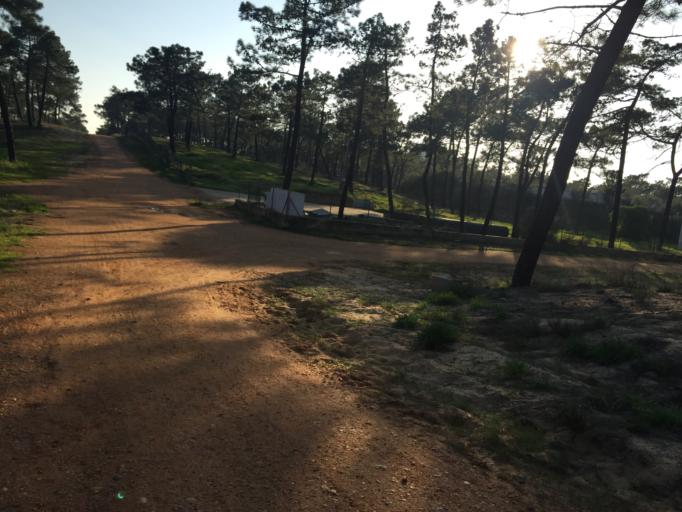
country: PT
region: Faro
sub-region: Vila Real de Santo Antonio
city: Monte Gordo
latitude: 37.1840
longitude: -7.4409
